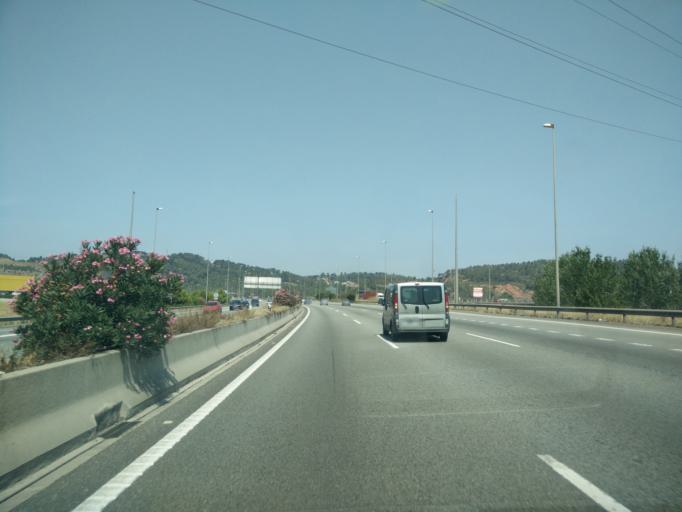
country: ES
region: Catalonia
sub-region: Provincia de Barcelona
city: Castellbisbal
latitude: 41.4681
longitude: 1.9668
